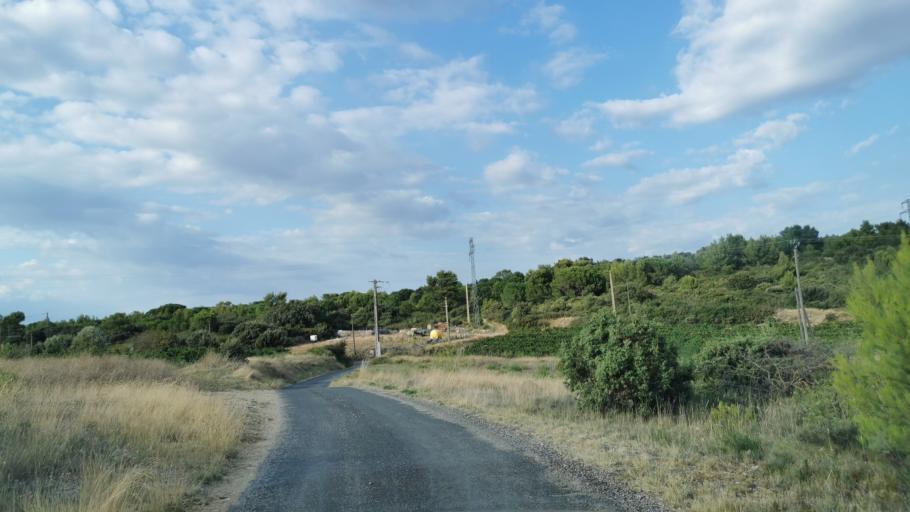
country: FR
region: Languedoc-Roussillon
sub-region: Departement de l'Aude
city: Bizanet
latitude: 43.1736
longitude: 2.8919
